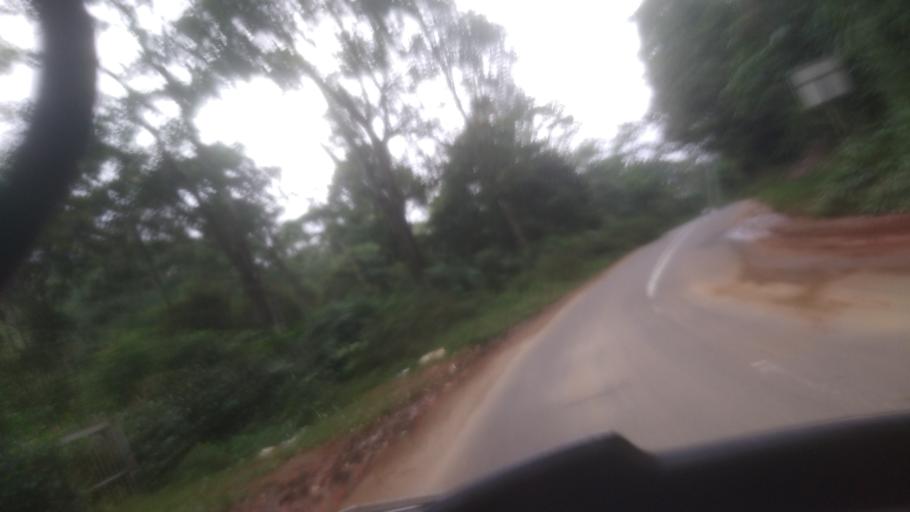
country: IN
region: Tamil Nadu
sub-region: Theni
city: Kombai
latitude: 9.8940
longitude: 77.1601
